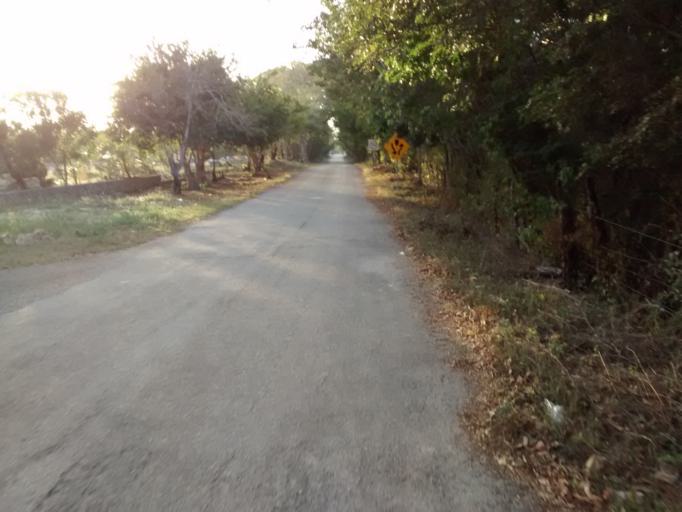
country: MX
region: Yucatan
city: Valladolid
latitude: 20.6809
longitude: -88.1620
